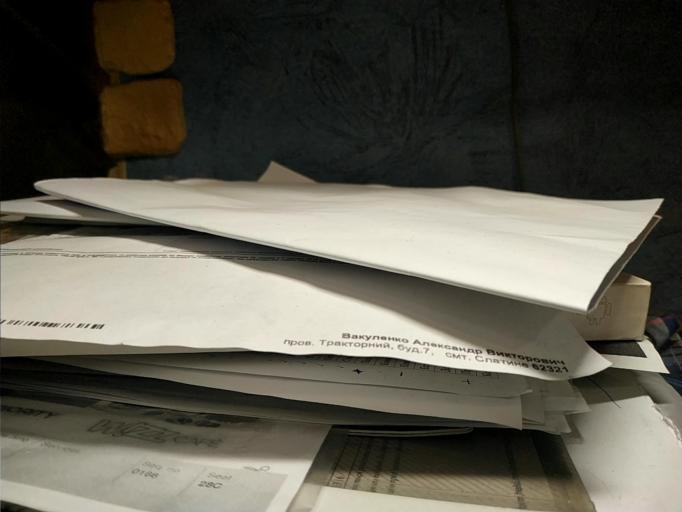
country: RU
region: Tverskaya
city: Zubtsov
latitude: 56.1012
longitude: 34.6821
